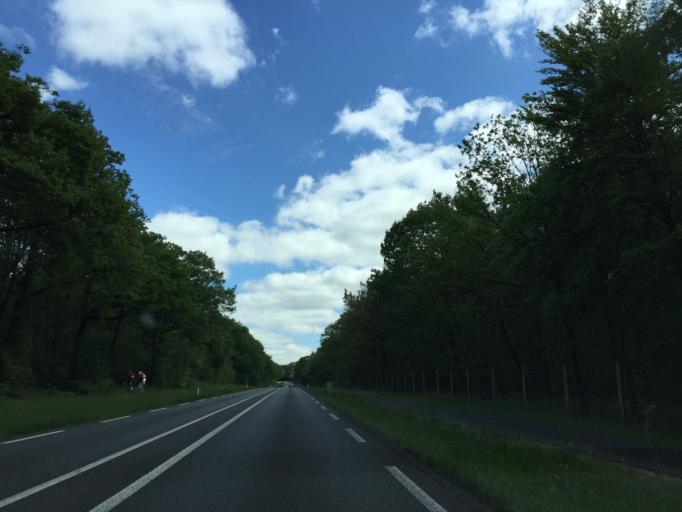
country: NL
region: Gelderland
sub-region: Gemeente Apeldoorn
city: Uddel
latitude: 52.2225
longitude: 5.8172
